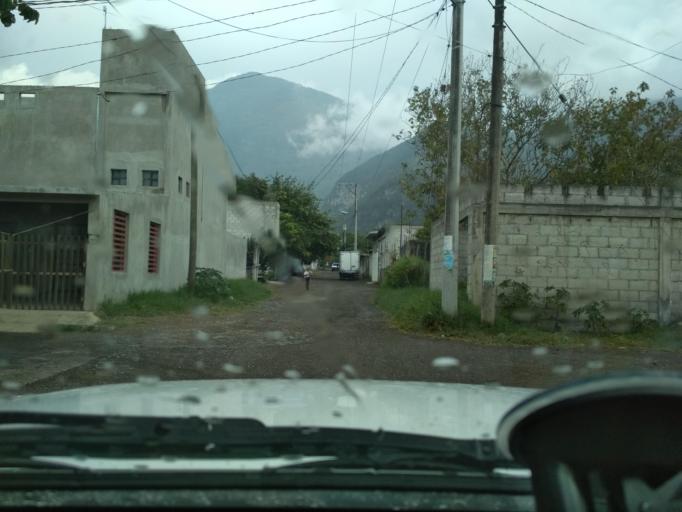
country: MX
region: Veracruz
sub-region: Nogales
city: Taza de Agua Ojo Zarco
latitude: 18.7804
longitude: -97.2050
